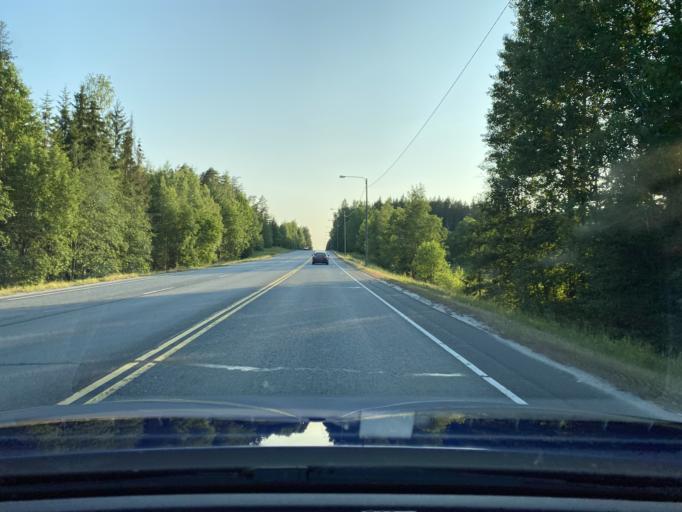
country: FI
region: Haeme
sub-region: Forssa
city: Forssa
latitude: 60.8287
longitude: 23.6538
